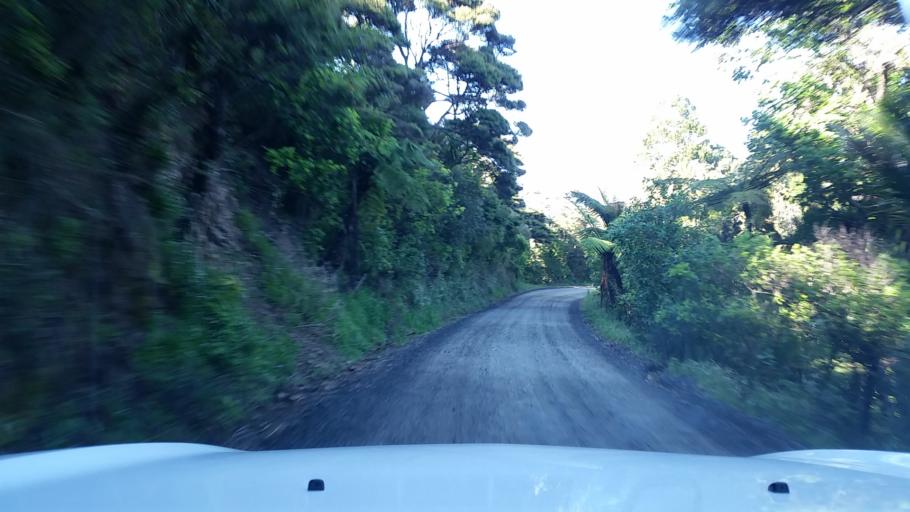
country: NZ
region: Auckland
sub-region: Auckland
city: Titirangi
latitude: -37.0301
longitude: 174.5252
